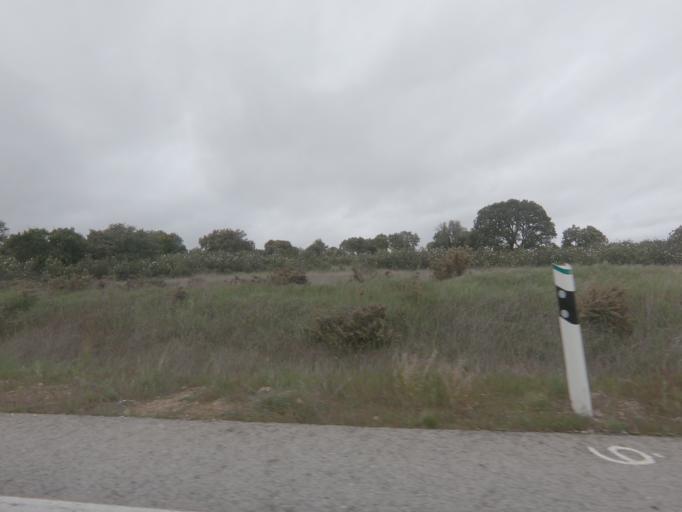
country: ES
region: Extremadura
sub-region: Provincia de Caceres
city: Malpartida de Caceres
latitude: 39.3110
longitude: -6.5113
